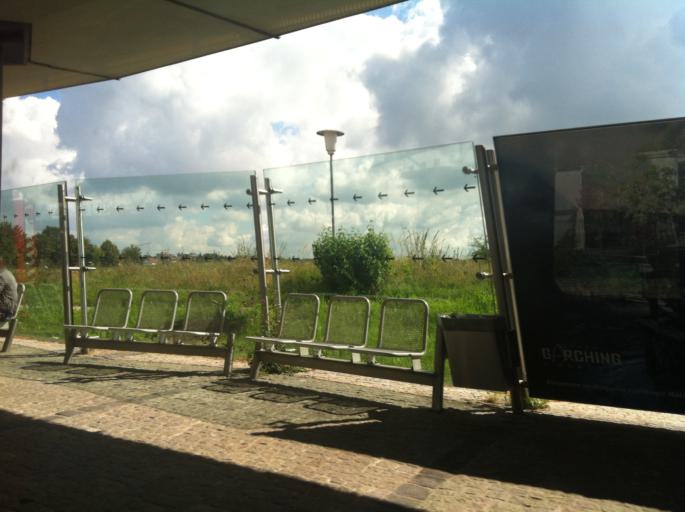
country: DE
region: Bavaria
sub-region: Upper Bavaria
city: Garching bei Munchen
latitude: 48.2471
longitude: 11.6309
